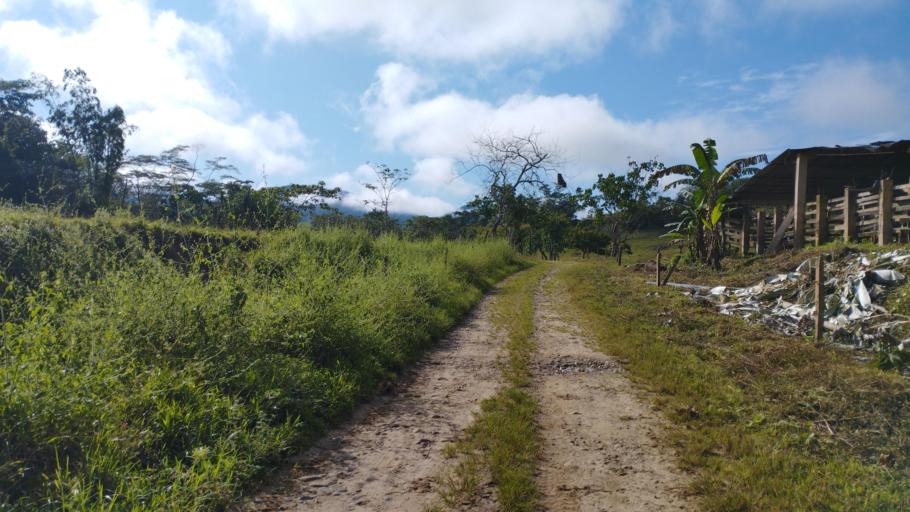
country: CO
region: Casanare
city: Sabanalarga
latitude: 4.7578
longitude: -73.0689
